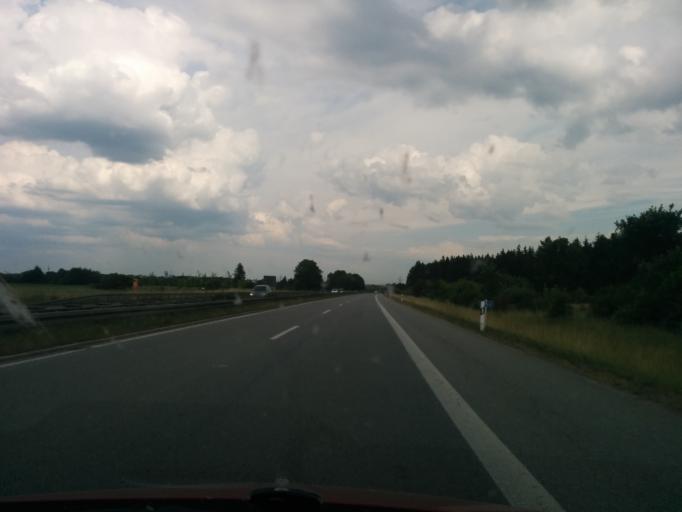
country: DE
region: Bavaria
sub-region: Swabia
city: Wiedergeltingen
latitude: 48.0272
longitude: 10.6809
